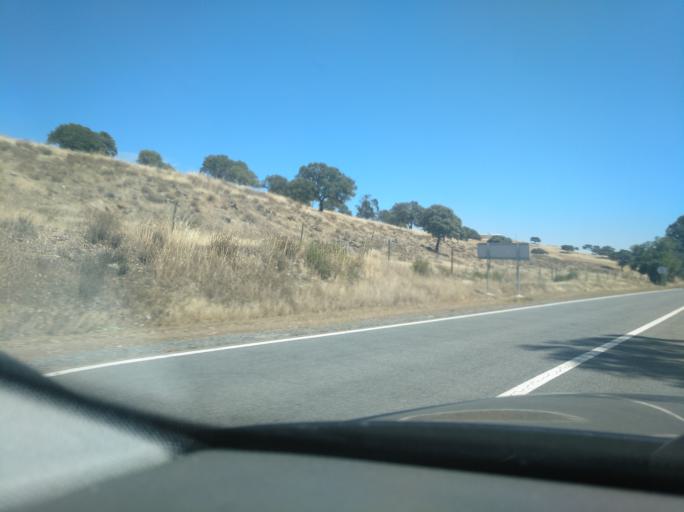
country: PT
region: Beja
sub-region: Castro Verde
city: Castro Verde
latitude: 37.6786
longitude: -8.0832
